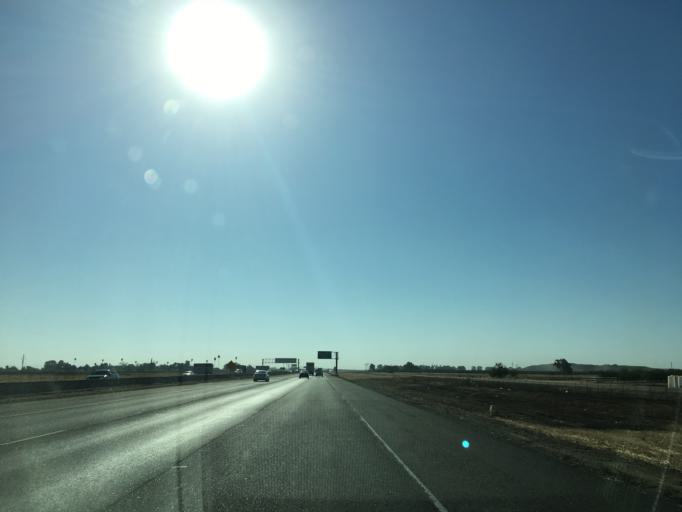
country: US
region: California
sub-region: Madera County
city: Fairmead
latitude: 37.0814
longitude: -120.2058
